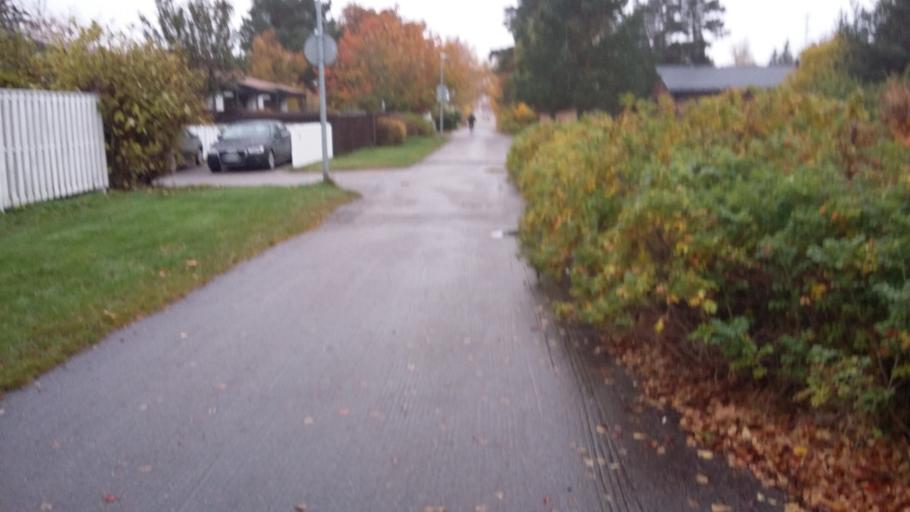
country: FI
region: Uusimaa
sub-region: Helsinki
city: Vantaa
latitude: 60.2966
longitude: 25.0290
